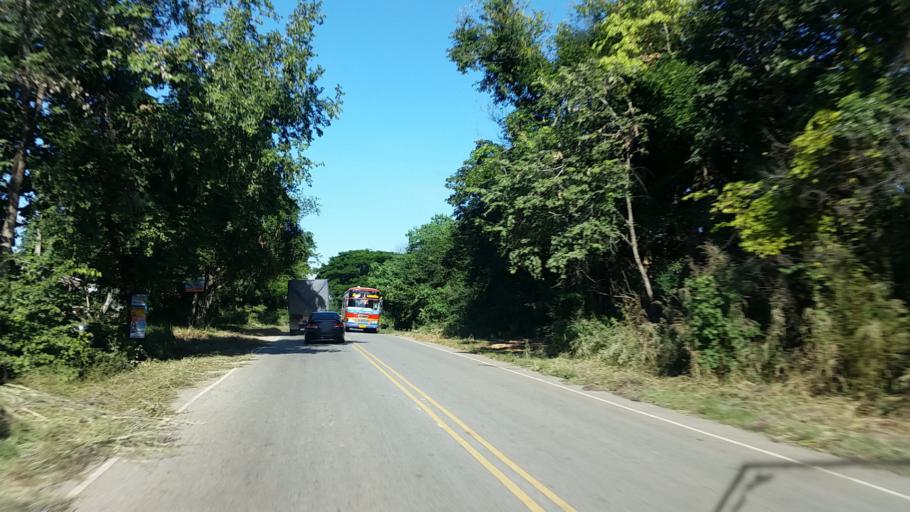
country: TH
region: Chaiyaphum
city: Thep Sathit
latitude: 15.5532
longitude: 101.4370
